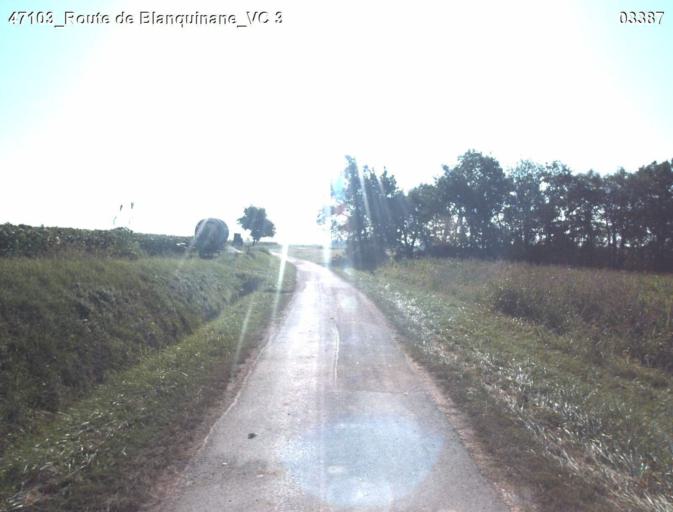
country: FR
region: Aquitaine
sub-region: Departement du Lot-et-Garonne
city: Nerac
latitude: 44.0903
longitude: 0.3259
